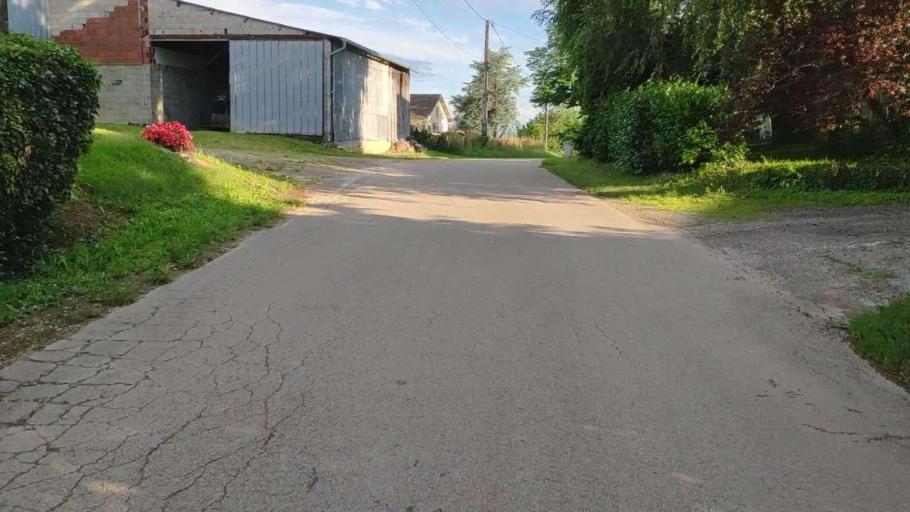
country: FR
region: Franche-Comte
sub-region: Departement du Jura
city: Bletterans
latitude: 46.7815
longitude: 5.4929
